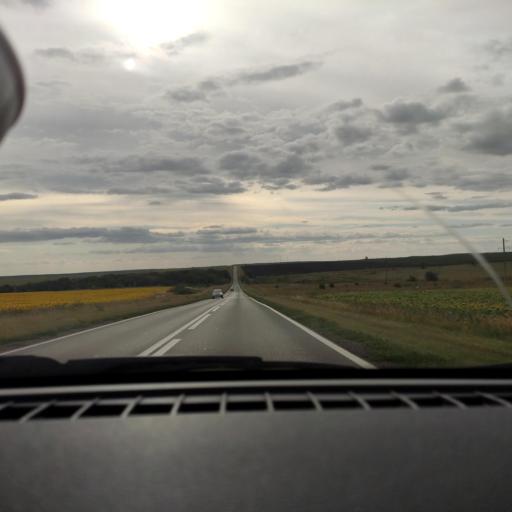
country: RU
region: Samara
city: Georgiyevka
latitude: 53.4172
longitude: 50.9155
